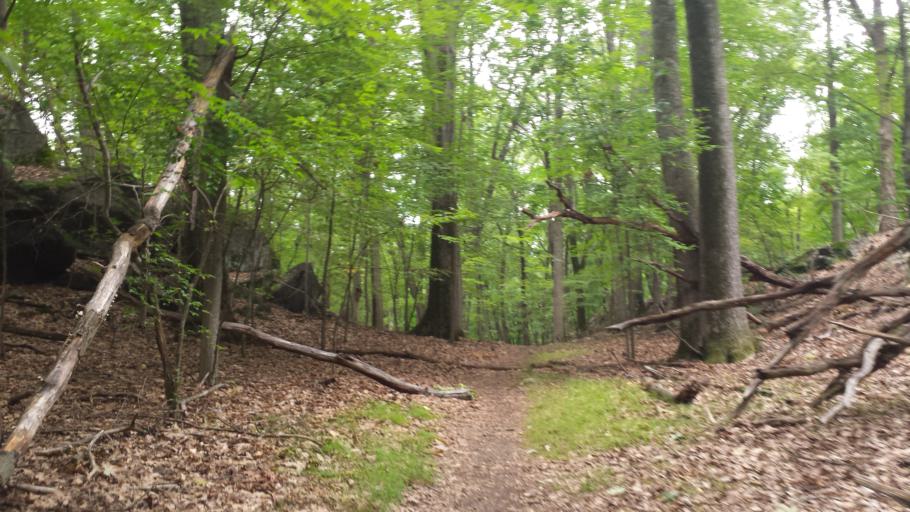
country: US
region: New York
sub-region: Westchester County
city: Buchanan
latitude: 41.2683
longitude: -73.9213
